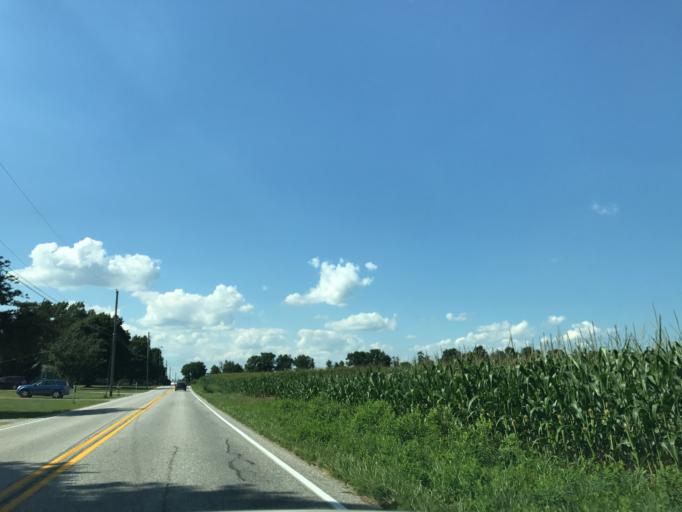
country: US
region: Pennsylvania
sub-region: York County
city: Pennville
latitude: 39.7737
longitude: -77.0247
